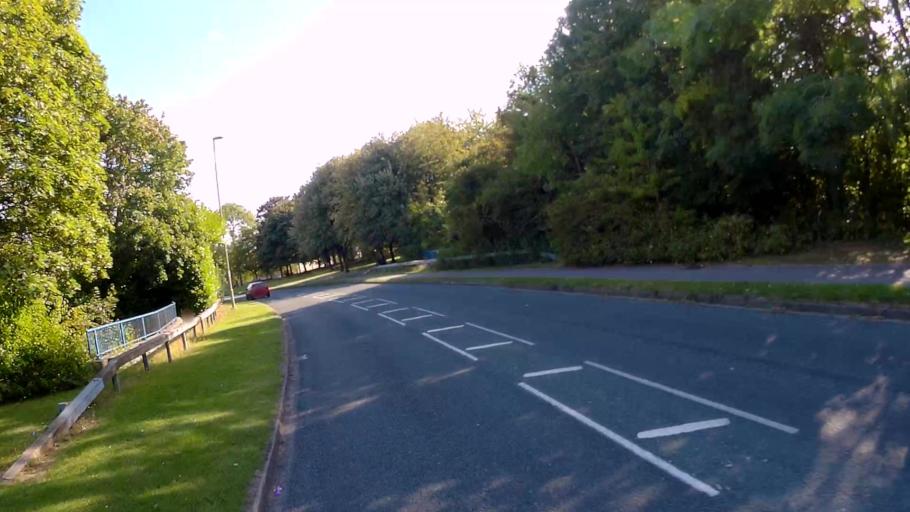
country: GB
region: England
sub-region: Hampshire
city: Basingstoke
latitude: 51.2430
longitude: -1.1176
